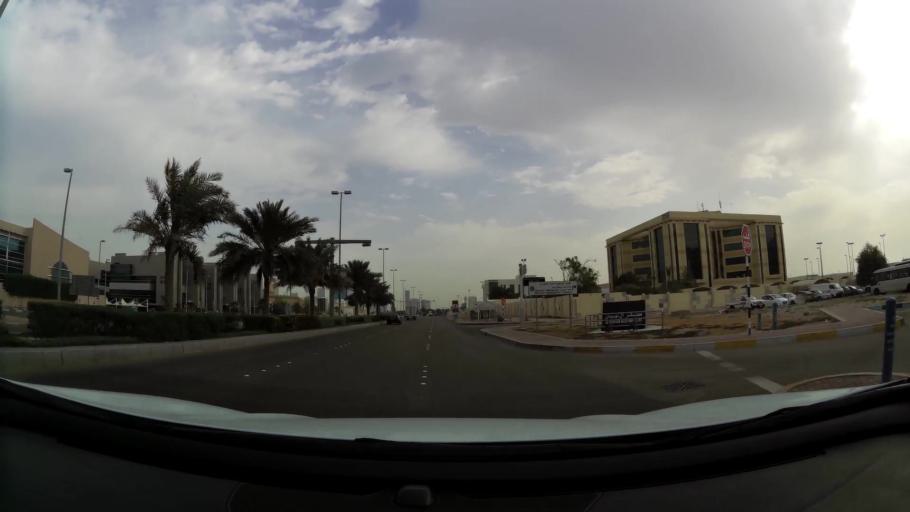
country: AE
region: Abu Dhabi
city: Abu Dhabi
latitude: 24.4693
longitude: 54.3854
